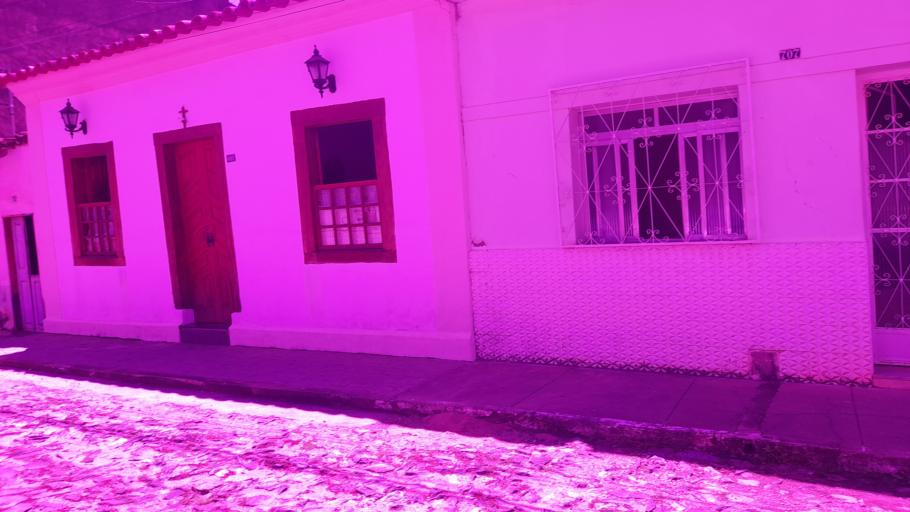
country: BR
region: Minas Gerais
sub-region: Sao Joao Del Rei
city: Sao Joao del Rei
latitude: -21.1383
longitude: -44.2694
